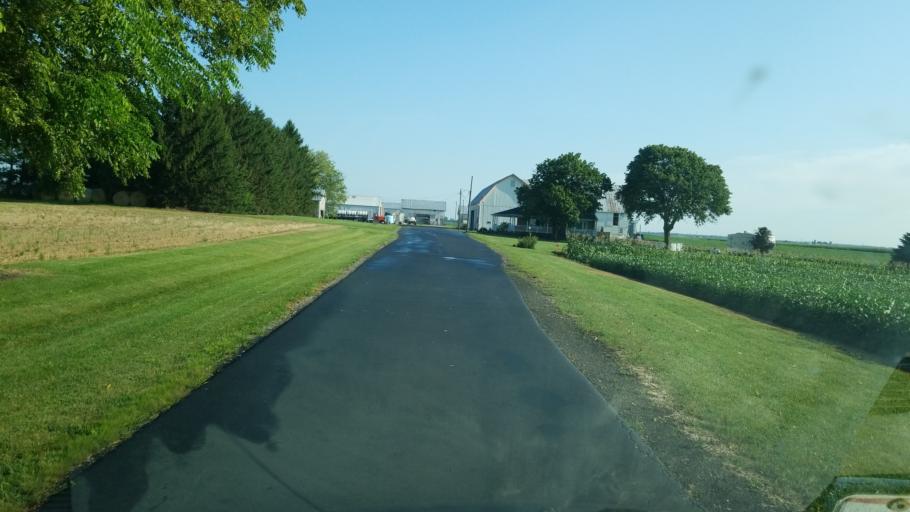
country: US
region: Ohio
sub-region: Crawford County
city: Bucyrus
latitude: 40.7771
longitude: -82.9177
